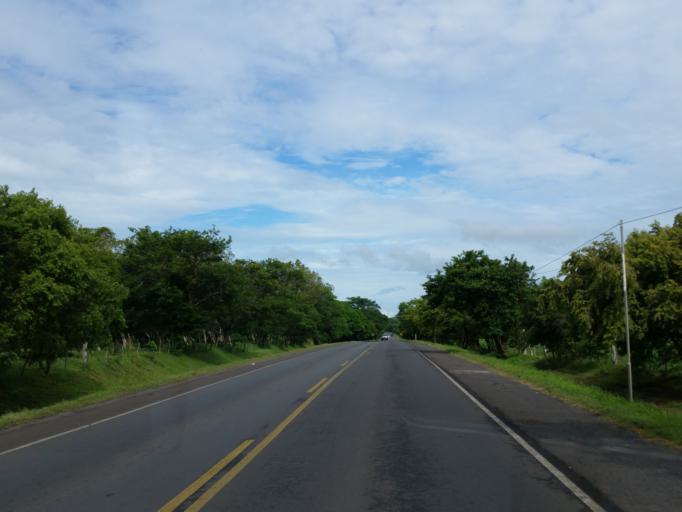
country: NI
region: Leon
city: Nagarote
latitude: 12.3097
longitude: -86.6036
